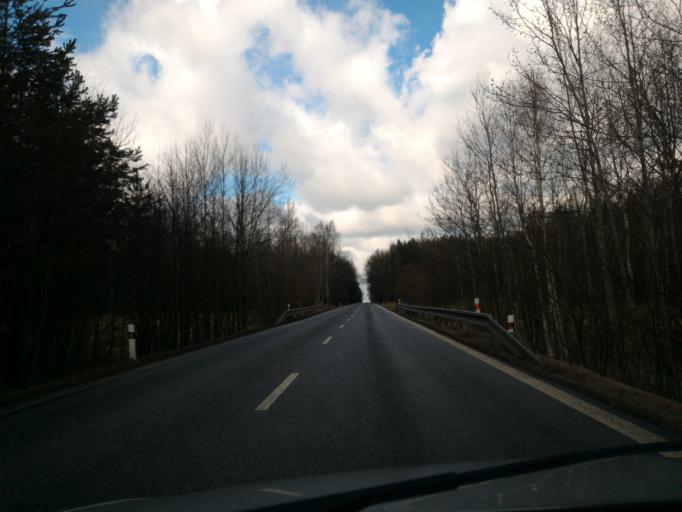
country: PL
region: Silesian Voivodeship
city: Zawidow
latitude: 50.9966
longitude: 15.0744
